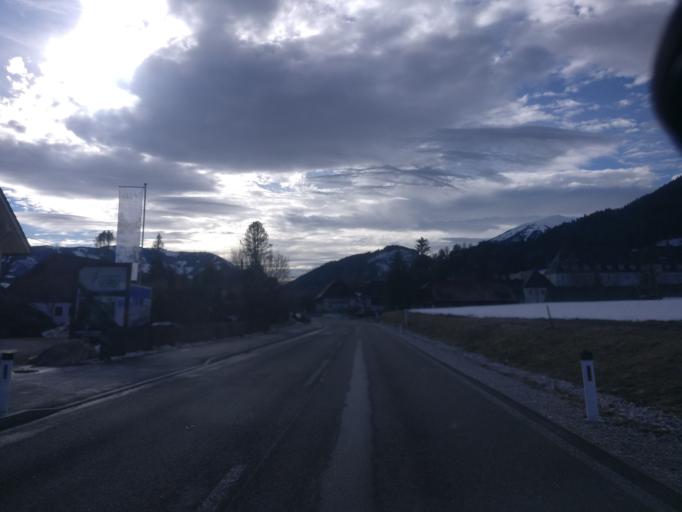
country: AT
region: Styria
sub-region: Politischer Bezirk Liezen
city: Hall bei Admont
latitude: 47.5942
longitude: 14.4941
